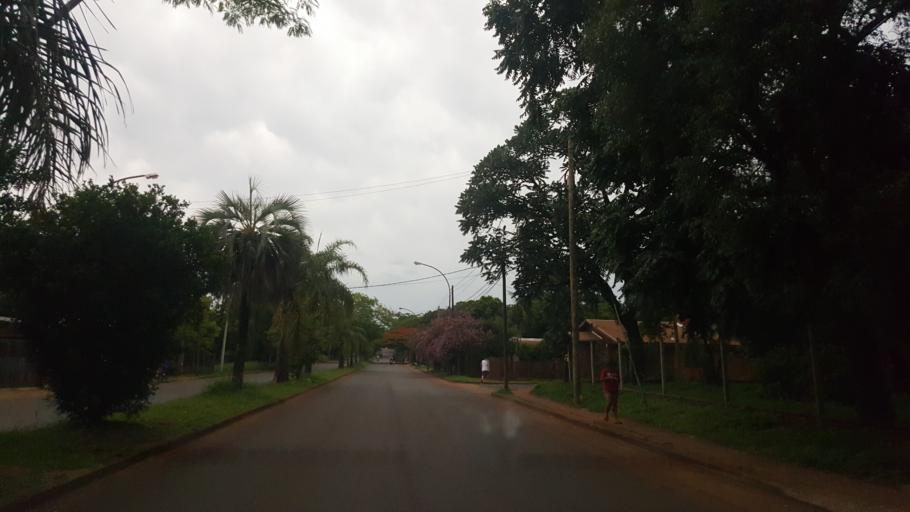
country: AR
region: Misiones
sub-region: Departamento de Capital
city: Posadas
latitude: -27.3617
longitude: -55.9310
